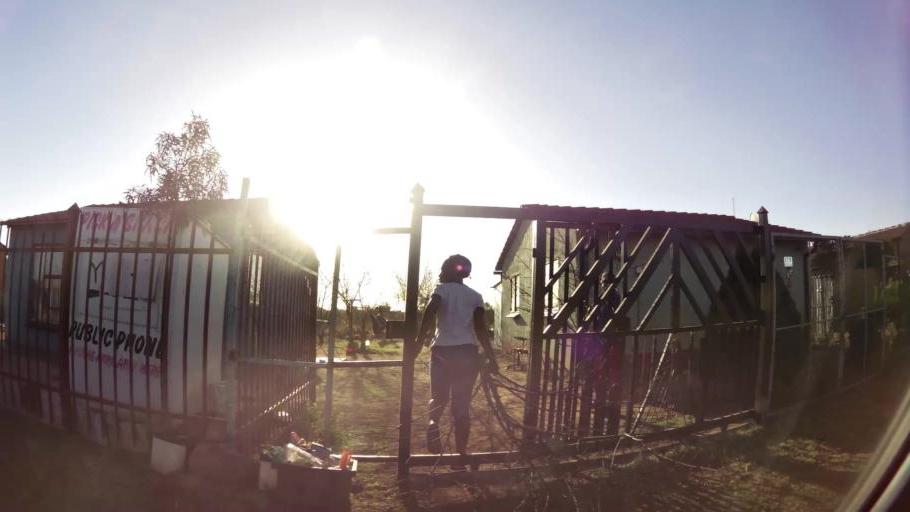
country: ZA
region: Gauteng
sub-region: City of Tshwane Metropolitan Municipality
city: Mabopane
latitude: -25.5964
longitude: 28.1018
